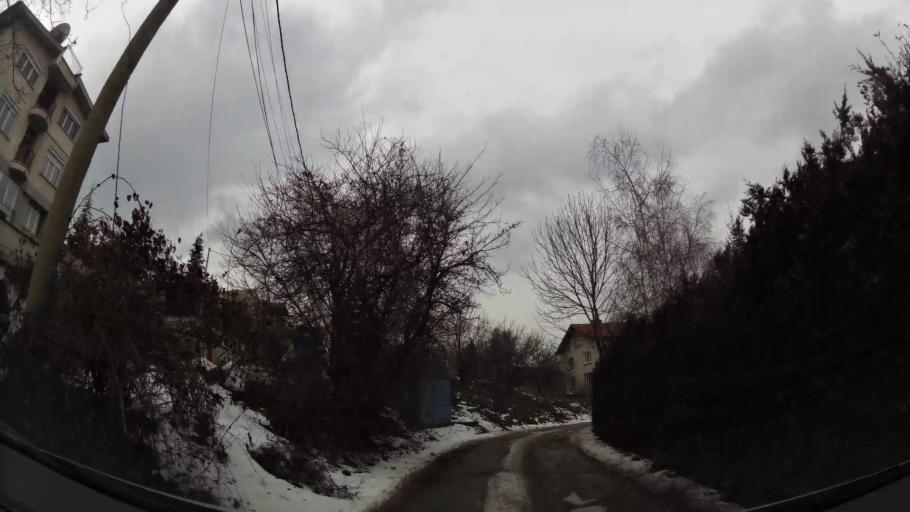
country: BG
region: Sofiya
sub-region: Obshtina Bozhurishte
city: Bozhurishte
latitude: 42.6792
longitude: 23.2314
